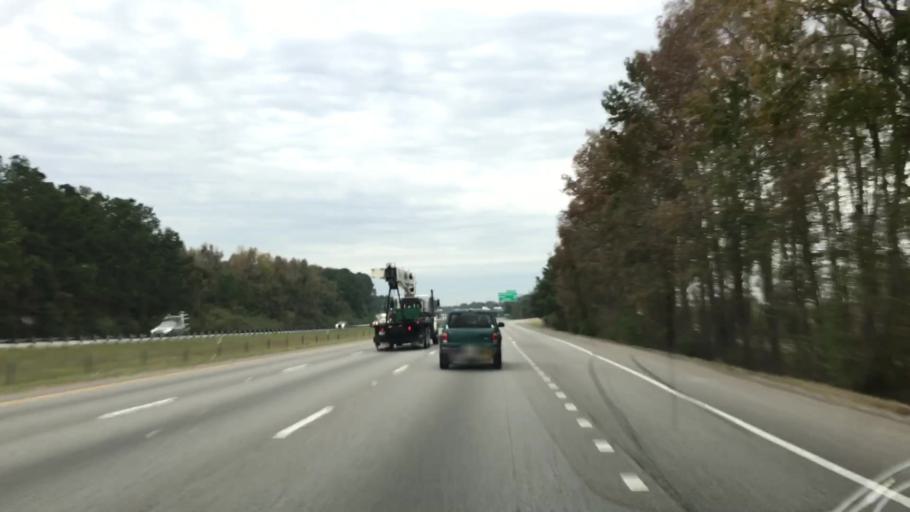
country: US
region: South Carolina
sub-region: Berkeley County
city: Ladson
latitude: 32.9940
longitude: -80.0889
